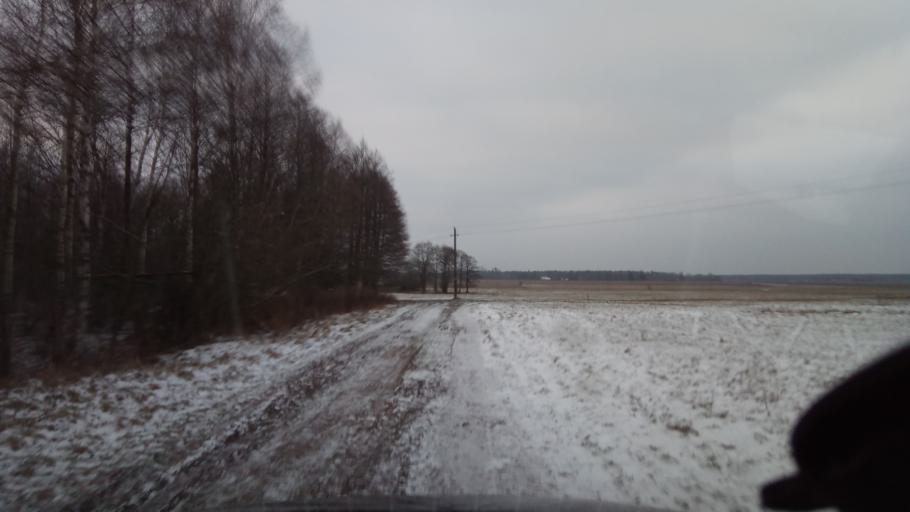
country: LT
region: Alytaus apskritis
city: Varena
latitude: 54.1172
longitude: 24.7165
